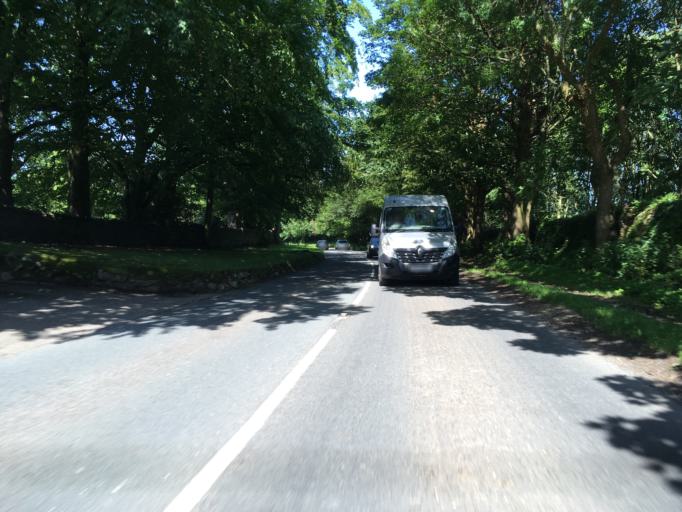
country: GB
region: England
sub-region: Gloucestershire
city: Stow on the Wold
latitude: 51.9304
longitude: -1.7287
